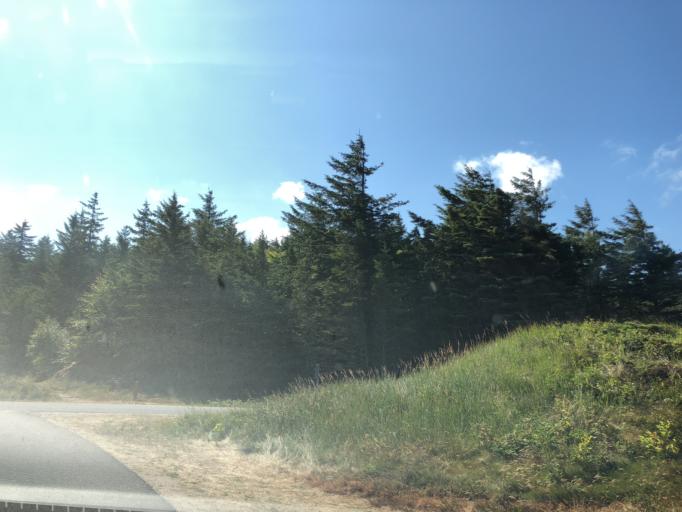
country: DK
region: North Denmark
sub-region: Jammerbugt Kommune
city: Fjerritslev
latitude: 57.1521
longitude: 9.3286
